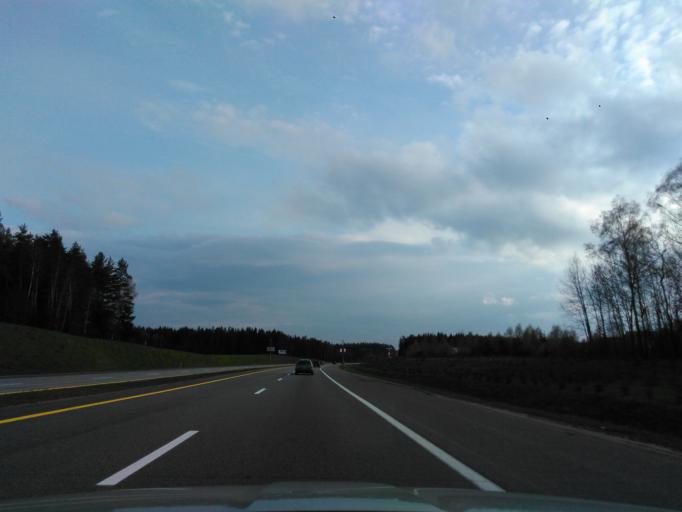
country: BY
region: Minsk
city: Astrashytski Haradok
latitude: 54.0469
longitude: 27.7012
